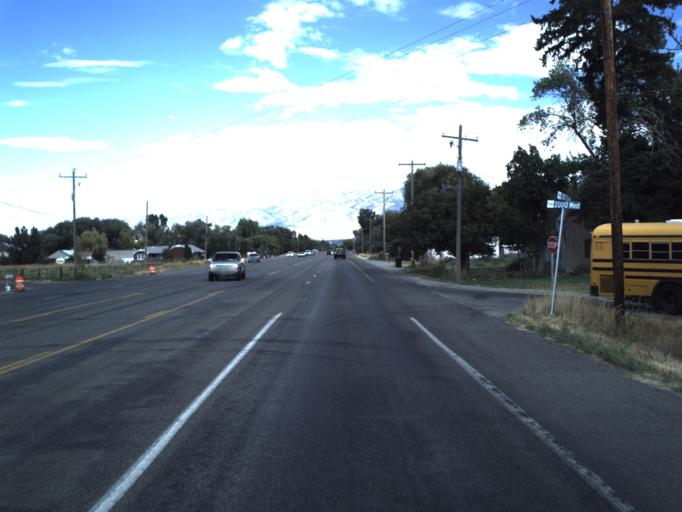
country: US
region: Utah
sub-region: Cache County
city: Nibley
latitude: 41.6767
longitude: -111.8817
